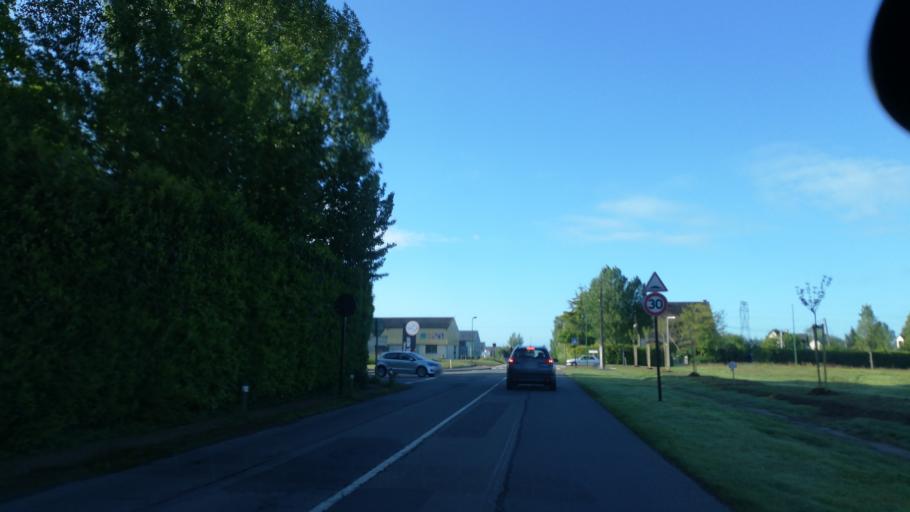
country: FR
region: Brittany
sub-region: Departement d'Ille-et-Vilaine
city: Irodouer
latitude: 48.2447
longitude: -1.9491
